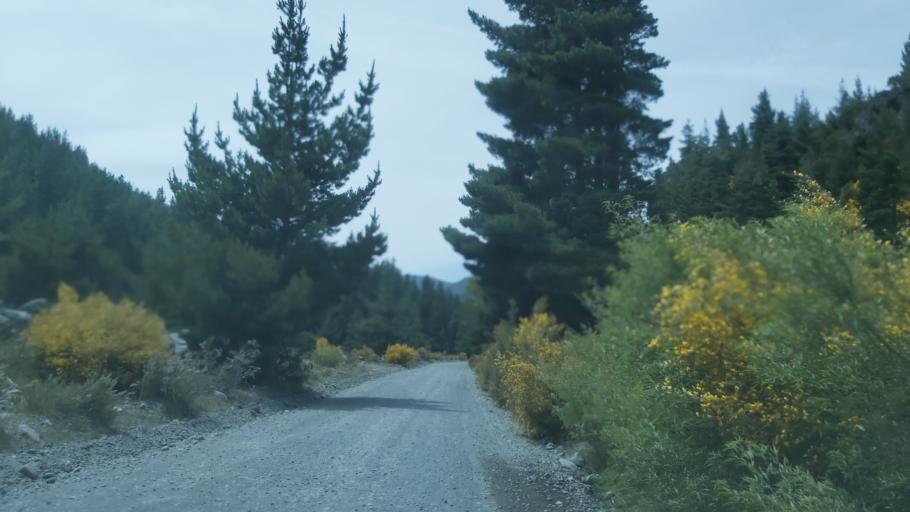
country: AR
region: Neuquen
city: Las Ovejas
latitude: -37.3915
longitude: -71.4646
